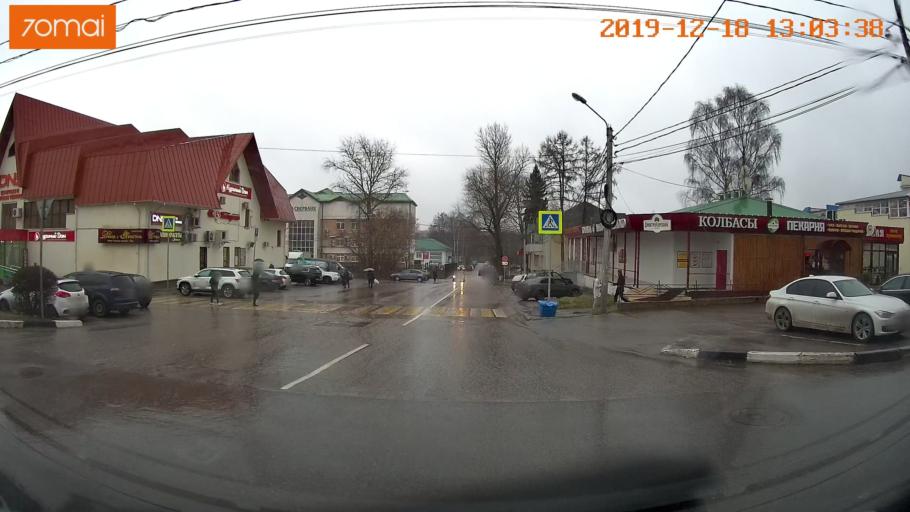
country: RU
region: Moskovskaya
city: Klin
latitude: 56.3330
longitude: 36.7311
